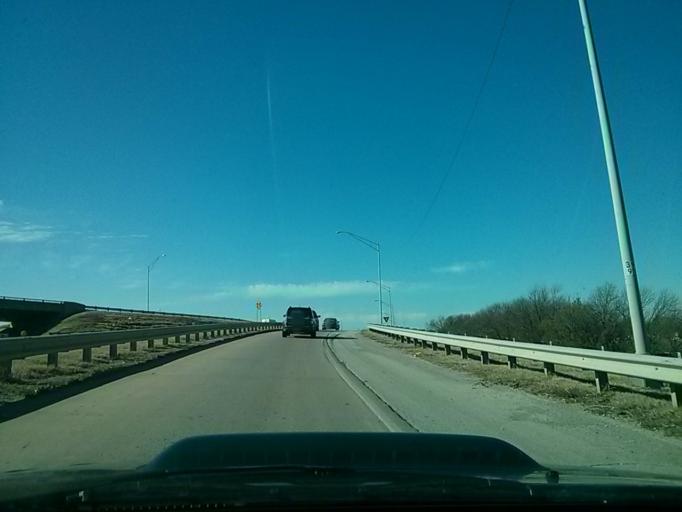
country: US
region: Oklahoma
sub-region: Tulsa County
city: Owasso
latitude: 36.1670
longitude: -95.8620
